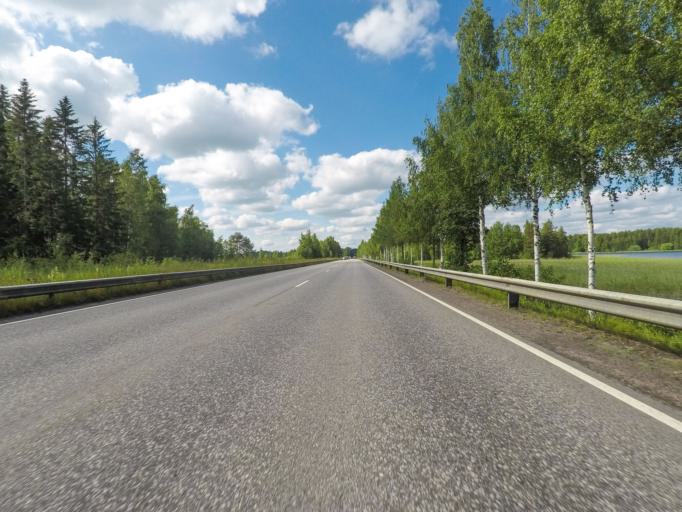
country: FI
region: Southern Savonia
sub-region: Savonlinna
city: Kerimaeki
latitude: 61.8136
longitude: 29.2640
